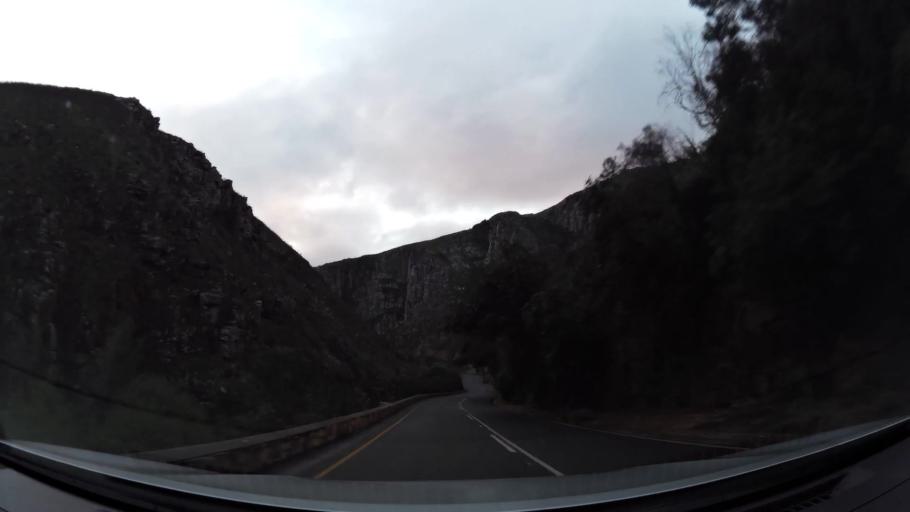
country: ZA
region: Western Cape
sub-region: Overberg District Municipality
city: Swellendam
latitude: -33.9587
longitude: 20.7077
